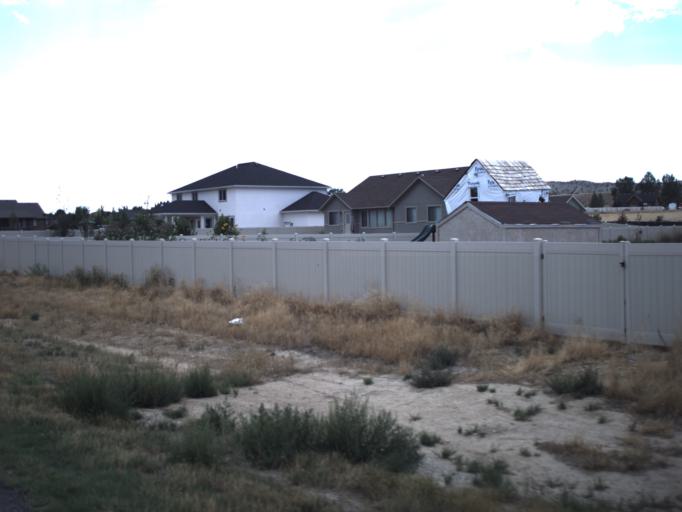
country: US
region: Utah
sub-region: Sanpete County
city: Centerfield
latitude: 39.1302
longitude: -111.7110
